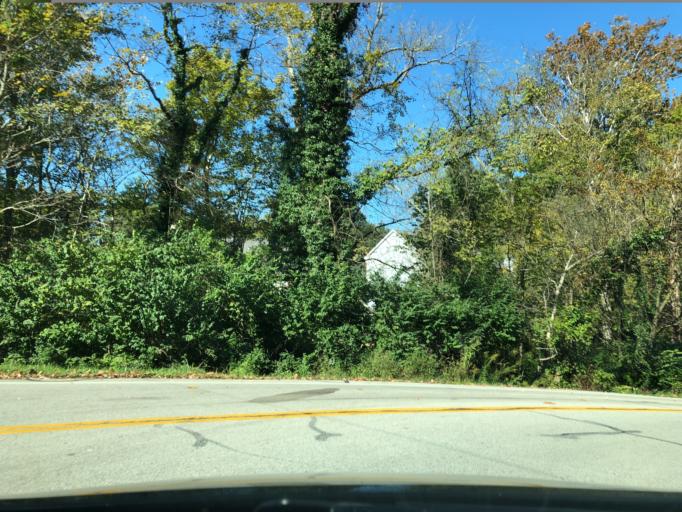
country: US
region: Ohio
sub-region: Hamilton County
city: Sixteen Mile Stand
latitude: 39.2681
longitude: -84.3067
